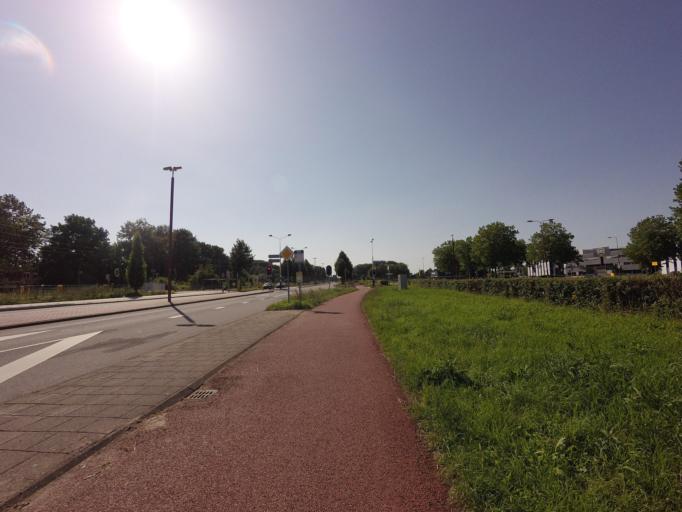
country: NL
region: Utrecht
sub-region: Gemeente Nieuwegein
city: Nieuwegein
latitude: 52.0461
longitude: 5.0902
